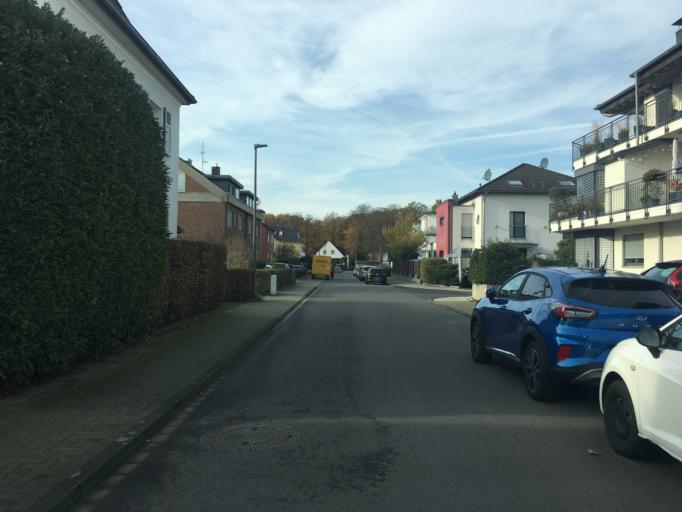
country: DE
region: North Rhine-Westphalia
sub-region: Regierungsbezirk Koln
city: Rath
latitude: 50.9531
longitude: 7.0985
